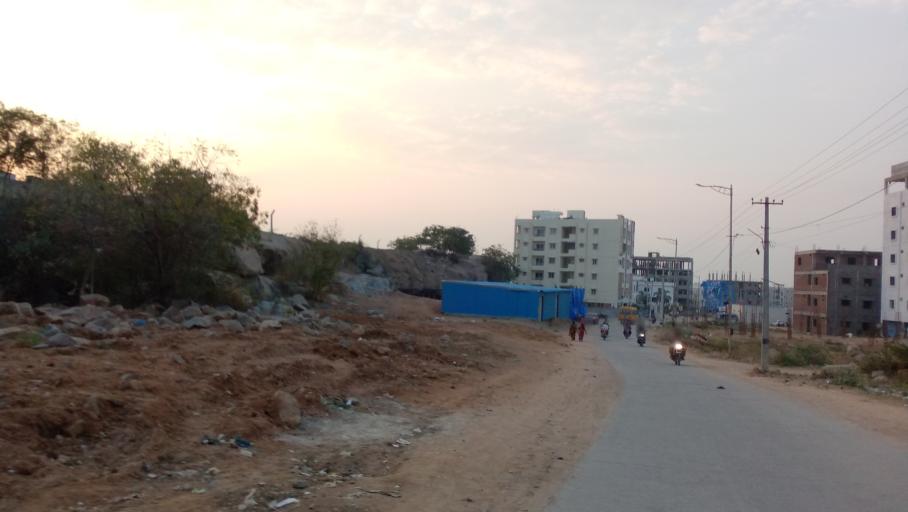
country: IN
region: Telangana
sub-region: Medak
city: Serilingampalle
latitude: 17.5209
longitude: 78.3036
